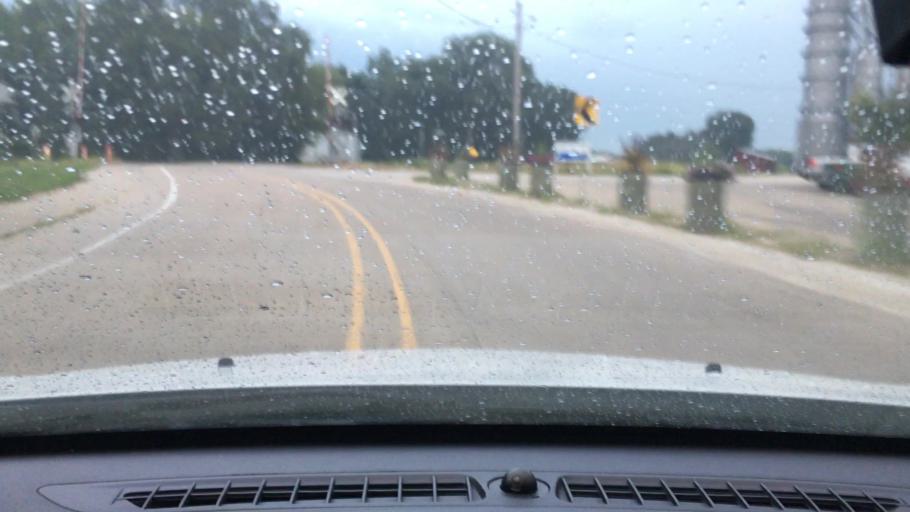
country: US
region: Illinois
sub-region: Ogle County
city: Rochelle
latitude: 41.8477
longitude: -89.0189
